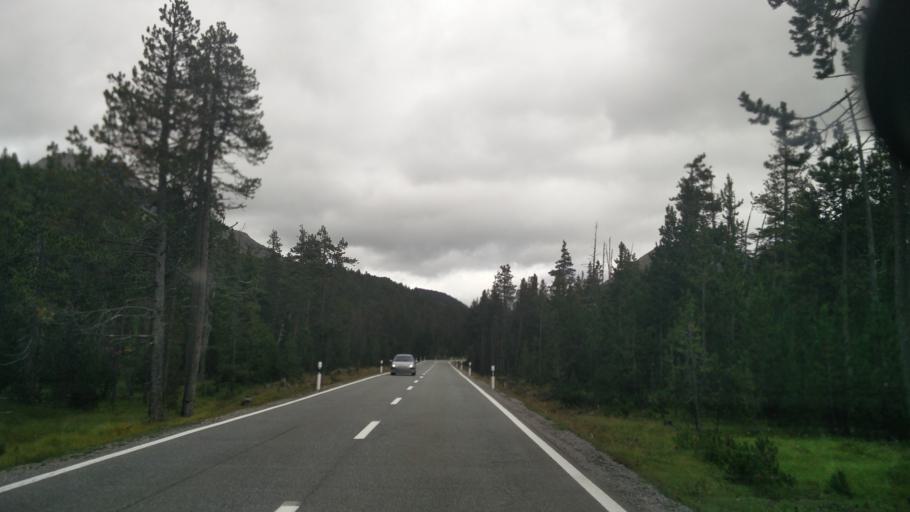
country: CH
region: Grisons
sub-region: Inn District
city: Scuol
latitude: 46.6517
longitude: 10.2593
